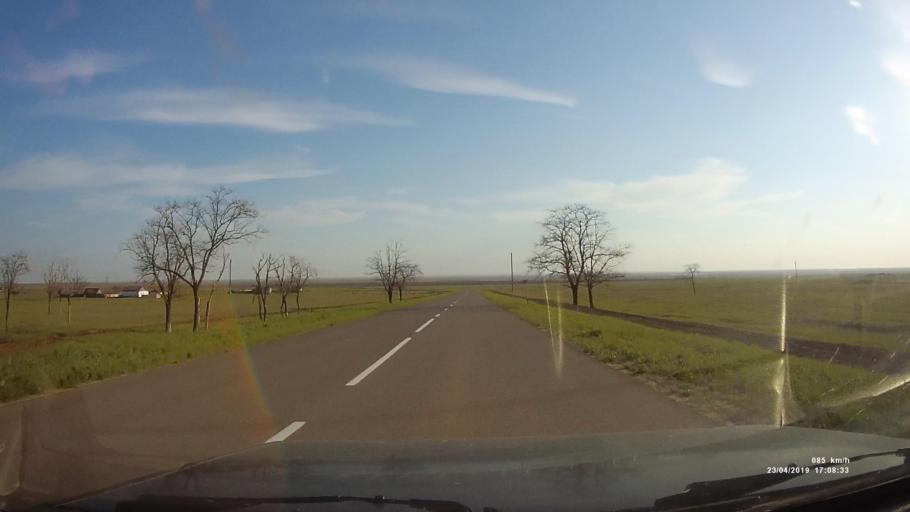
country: RU
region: Kalmykiya
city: Priyutnoye
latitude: 46.2699
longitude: 43.4868
